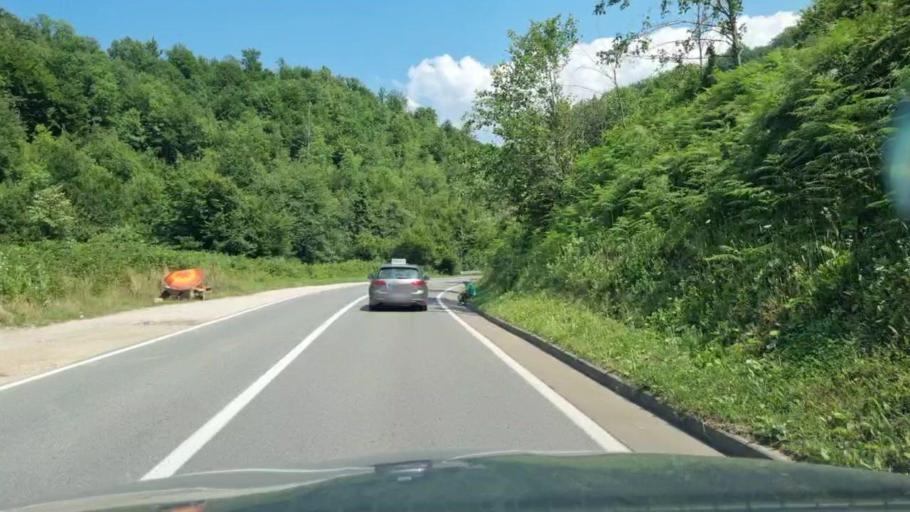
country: BA
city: Stupari
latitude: 44.3576
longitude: 18.6721
